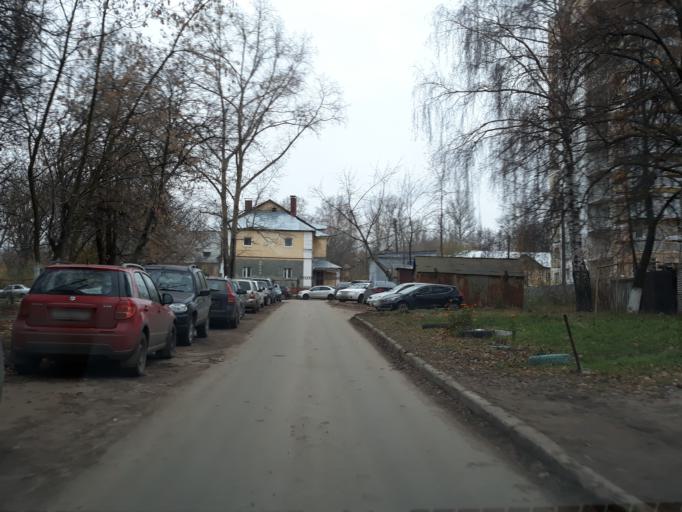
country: RU
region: Nizjnij Novgorod
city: Nizhniy Novgorod
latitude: 56.2488
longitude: 43.9774
